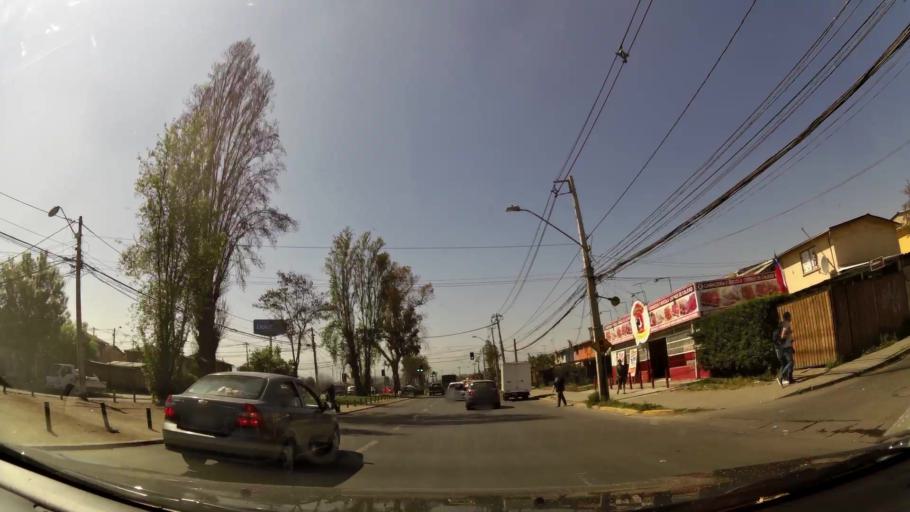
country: CL
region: Santiago Metropolitan
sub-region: Provincia de Santiago
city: Lo Prado
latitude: -33.3607
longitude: -70.7474
